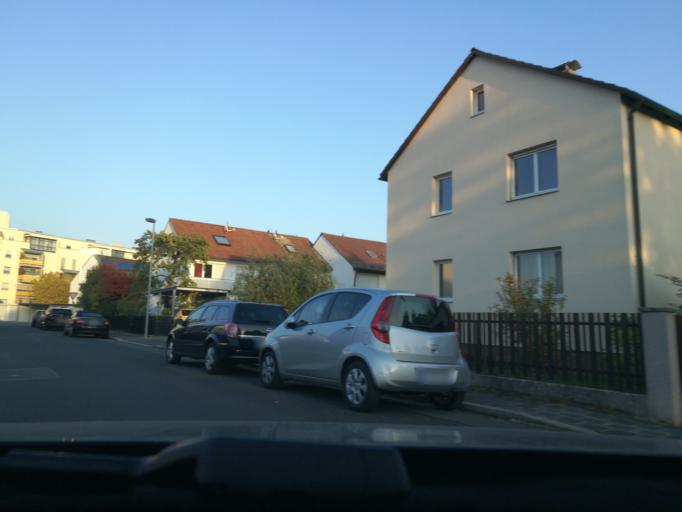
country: DE
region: Bavaria
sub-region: Regierungsbezirk Mittelfranken
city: Furth
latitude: 49.4918
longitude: 10.9935
